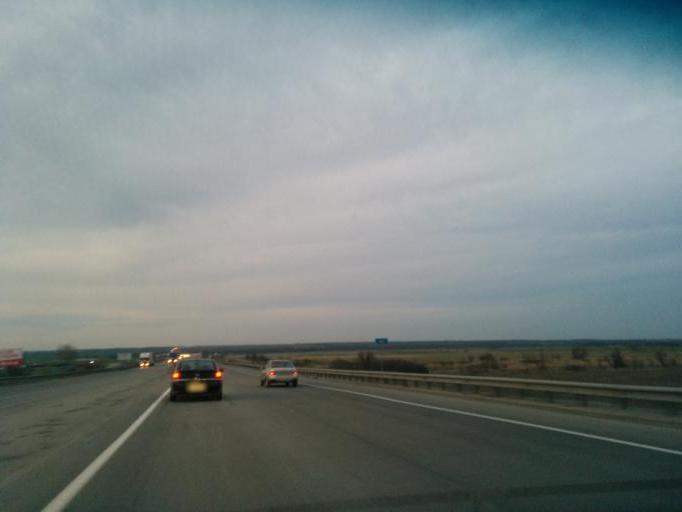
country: RU
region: Rostov
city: Grushevskaya
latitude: 47.4432
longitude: 39.9745
